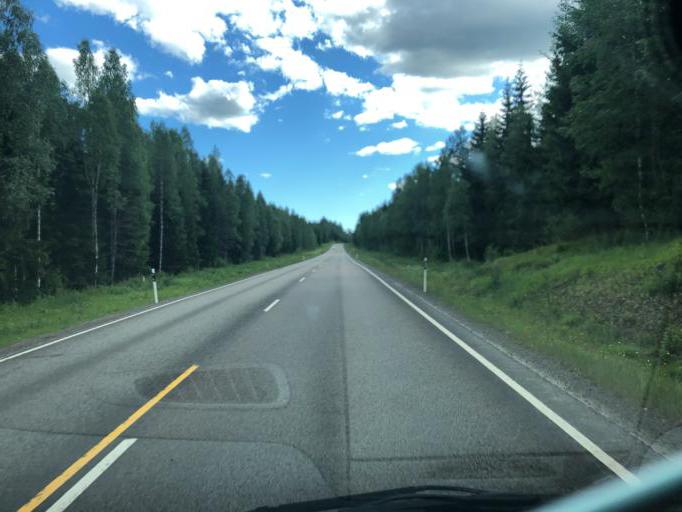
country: FI
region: Kymenlaakso
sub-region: Kouvola
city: Kouvola
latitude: 61.0135
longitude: 26.9515
